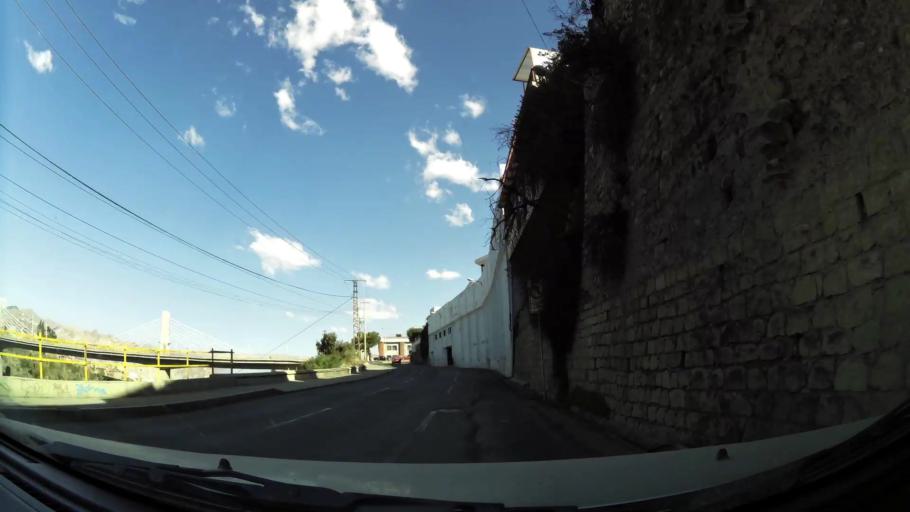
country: BO
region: La Paz
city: La Paz
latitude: -16.5154
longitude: -68.1186
